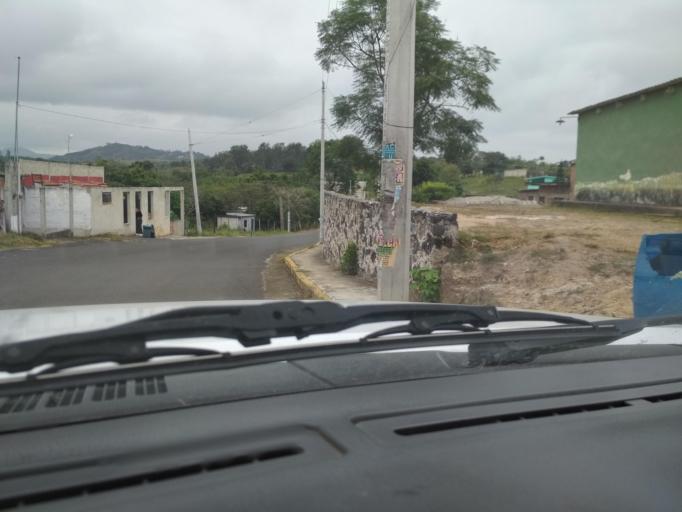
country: MX
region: Veracruz
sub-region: Emiliano Zapata
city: Dos Rios
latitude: 19.5256
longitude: -96.8008
